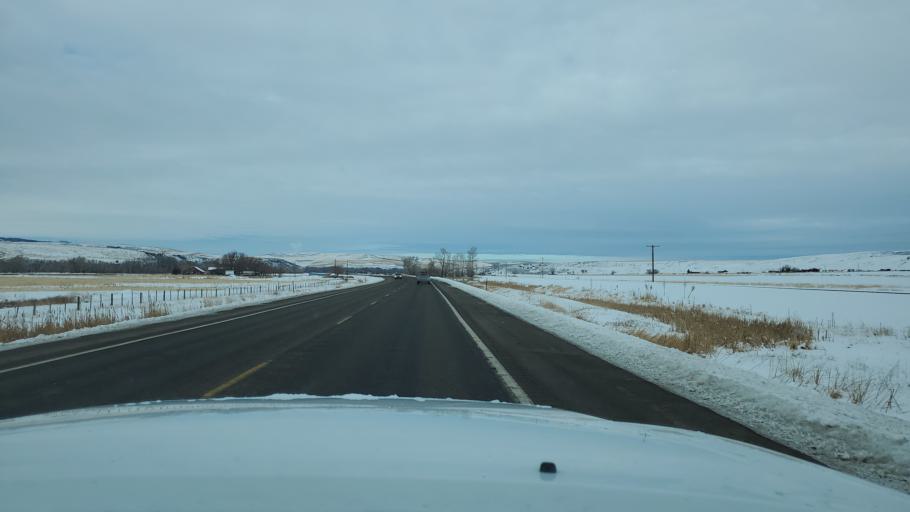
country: US
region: Colorado
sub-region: Routt County
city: Hayden
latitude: 40.4927
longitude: -107.3364
